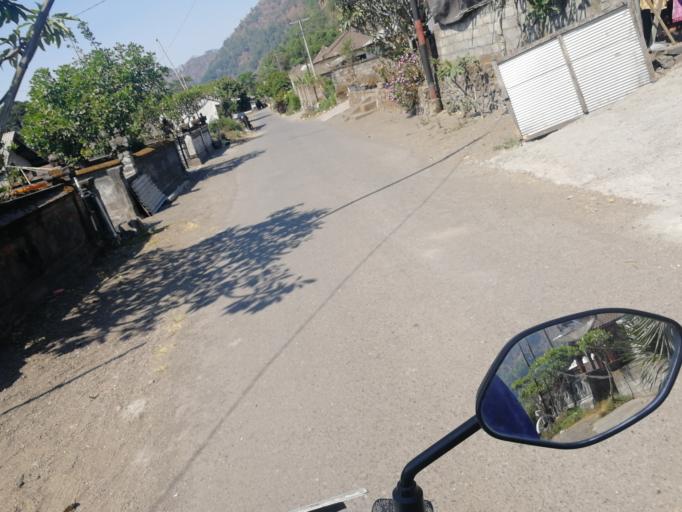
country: ID
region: Bali
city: Banjar Trunyan
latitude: -8.2752
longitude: 115.4137
